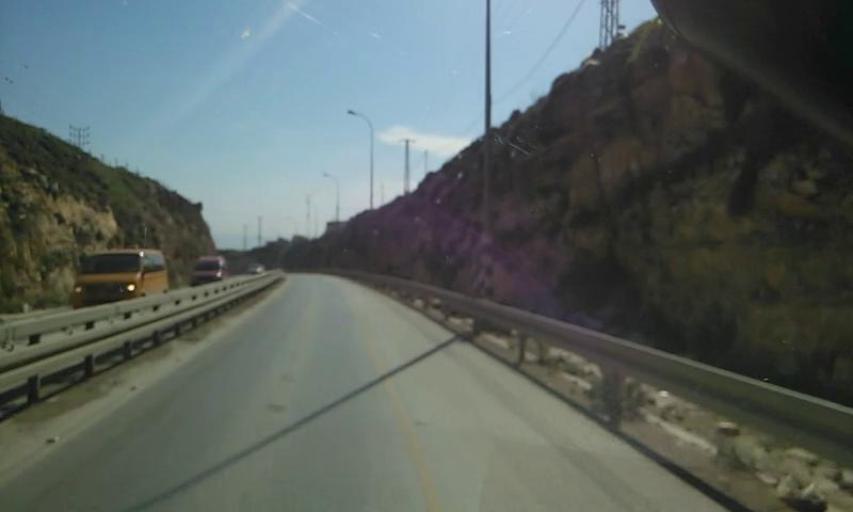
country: PS
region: West Bank
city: Jaba`
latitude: 31.8543
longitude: 35.2493
